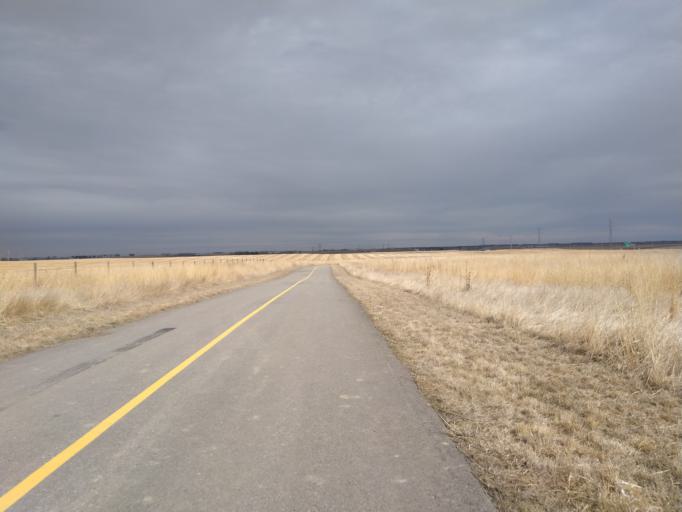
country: CA
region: Alberta
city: Airdrie
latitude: 51.1796
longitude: -114.0359
